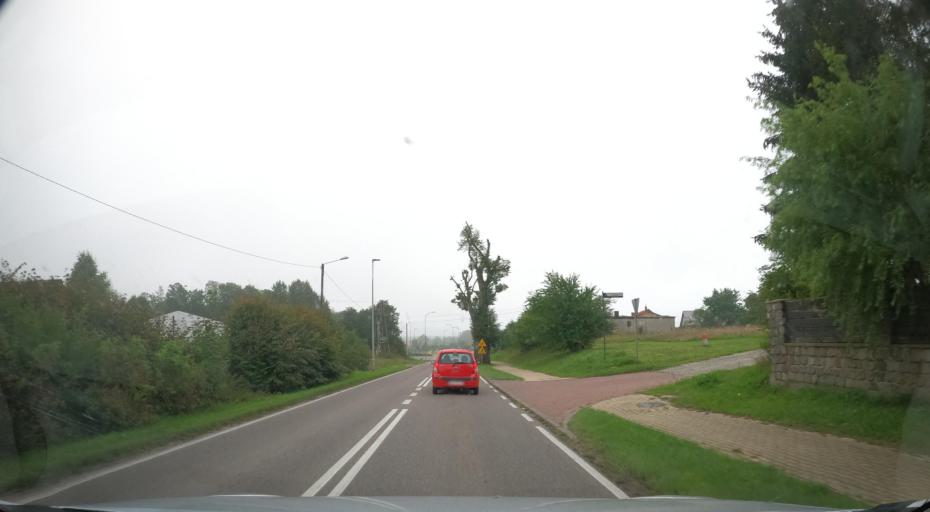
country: PL
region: Pomeranian Voivodeship
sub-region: Powiat wejherowski
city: Bojano
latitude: 54.4463
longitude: 18.3853
